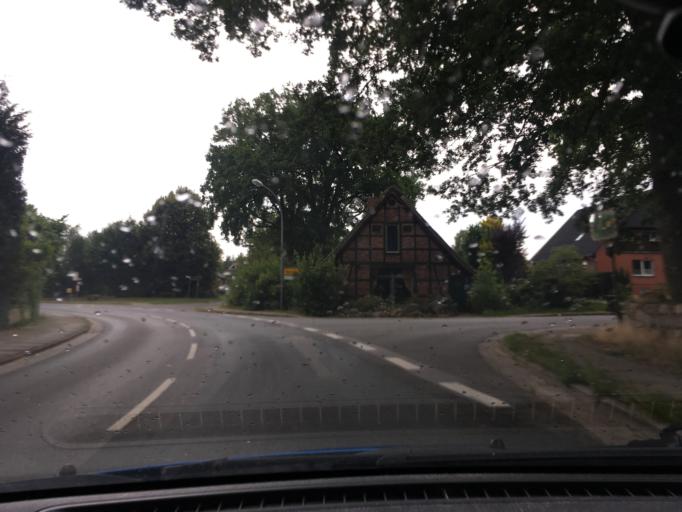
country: DE
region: Lower Saxony
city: Wenzendorf
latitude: 53.3478
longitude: 9.7561
